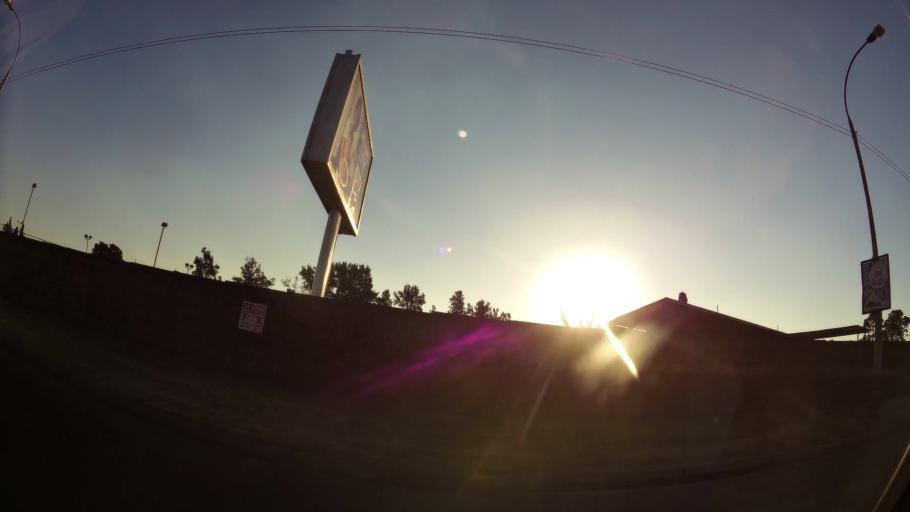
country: ZA
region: Gauteng
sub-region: Ekurhuleni Metropolitan Municipality
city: Germiston
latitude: -26.2676
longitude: 28.1260
